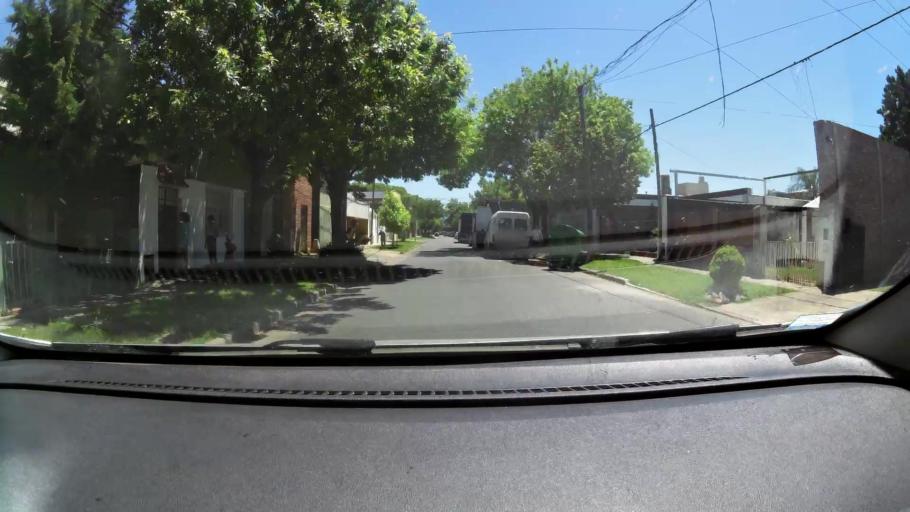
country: AR
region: Santa Fe
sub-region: Departamento de Rosario
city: Rosario
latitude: -32.9420
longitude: -60.7113
